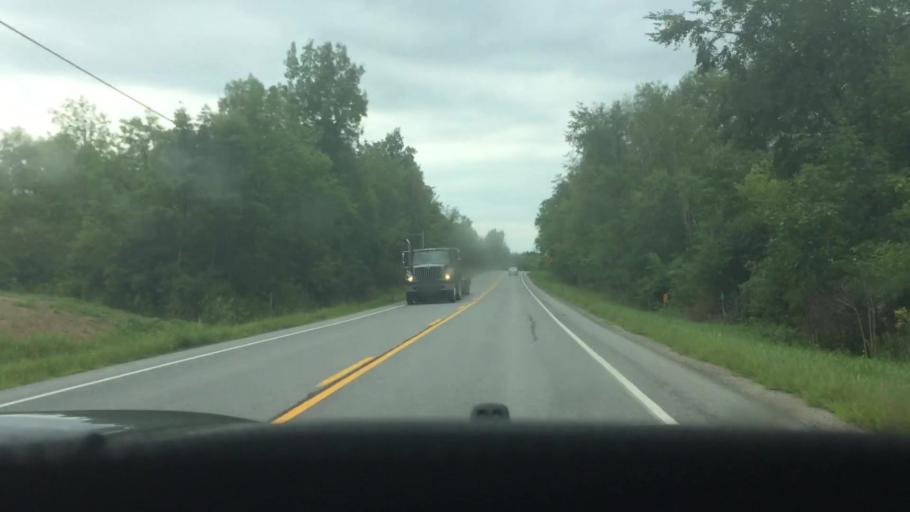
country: US
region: New York
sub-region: St. Lawrence County
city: Canton
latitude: 44.5088
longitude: -75.3399
